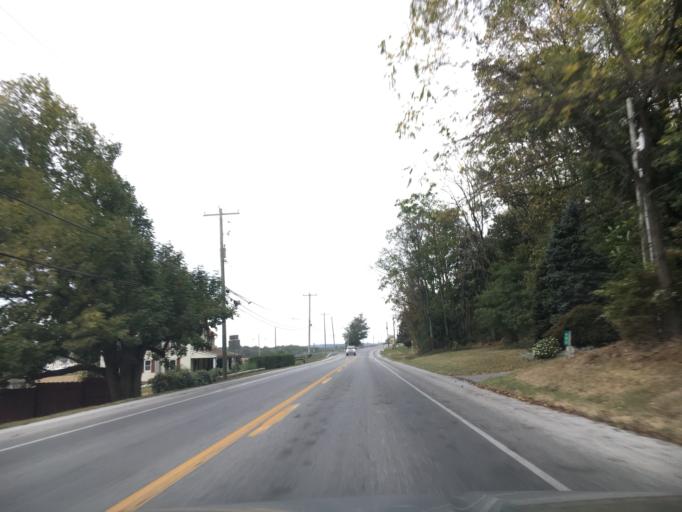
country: US
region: Pennsylvania
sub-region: Lancaster County
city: Quarryville
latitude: 39.9058
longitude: -76.1320
